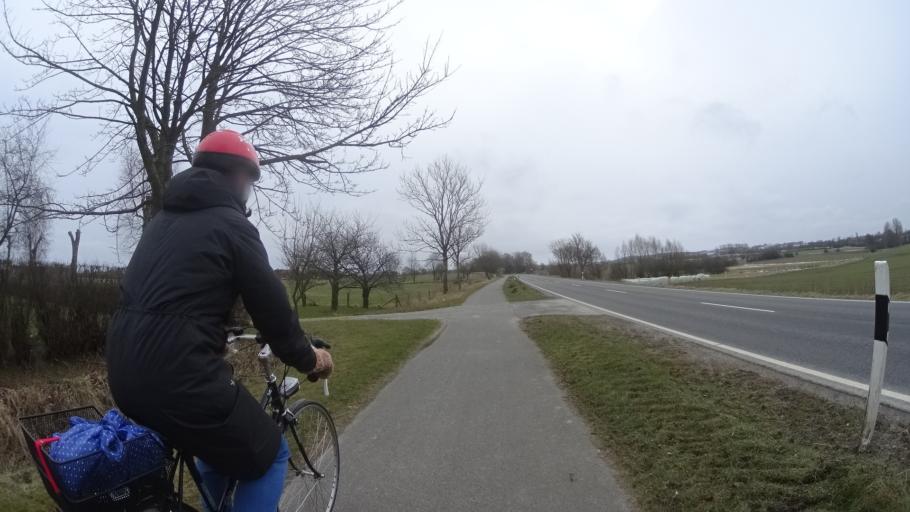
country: DE
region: Schleswig-Holstein
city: Hohenfelde
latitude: 54.3604
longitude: 10.5247
